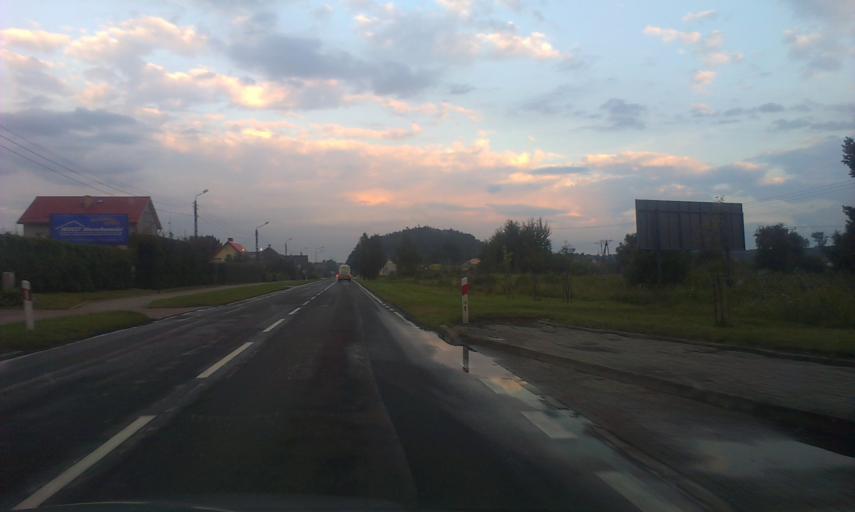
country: PL
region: West Pomeranian Voivodeship
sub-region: Powiat koszalinski
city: Sianow
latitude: 54.1323
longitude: 16.2882
